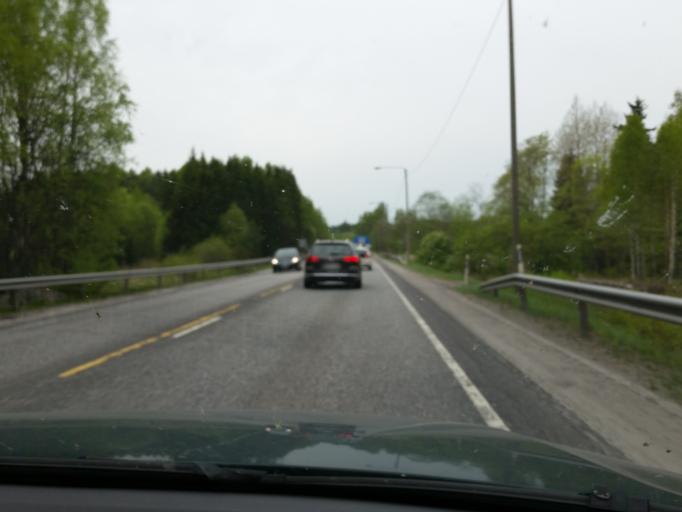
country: FI
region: Uusimaa
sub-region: Helsinki
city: Espoo
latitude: 60.2000
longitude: 24.5929
